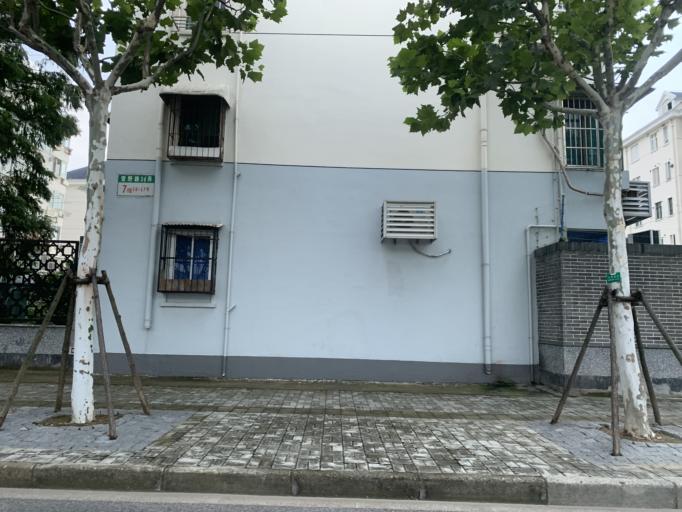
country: CN
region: Shanghai Shi
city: Luwan
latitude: 31.1836
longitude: 121.4922
